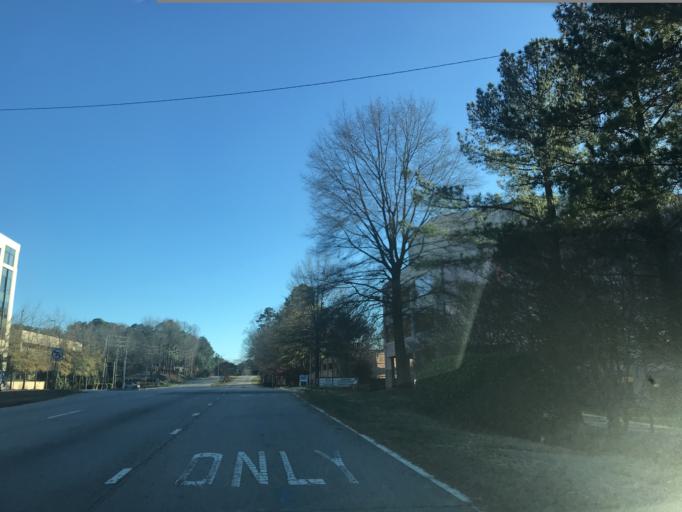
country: US
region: North Carolina
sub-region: Wake County
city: West Raleigh
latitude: 35.8317
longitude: -78.6674
